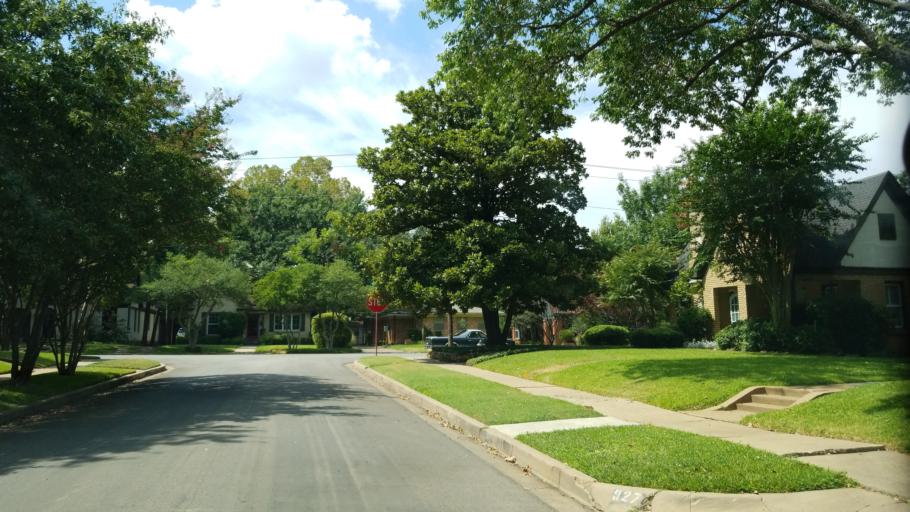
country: US
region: Texas
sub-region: Dallas County
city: Dallas
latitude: 32.7561
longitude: -96.8387
